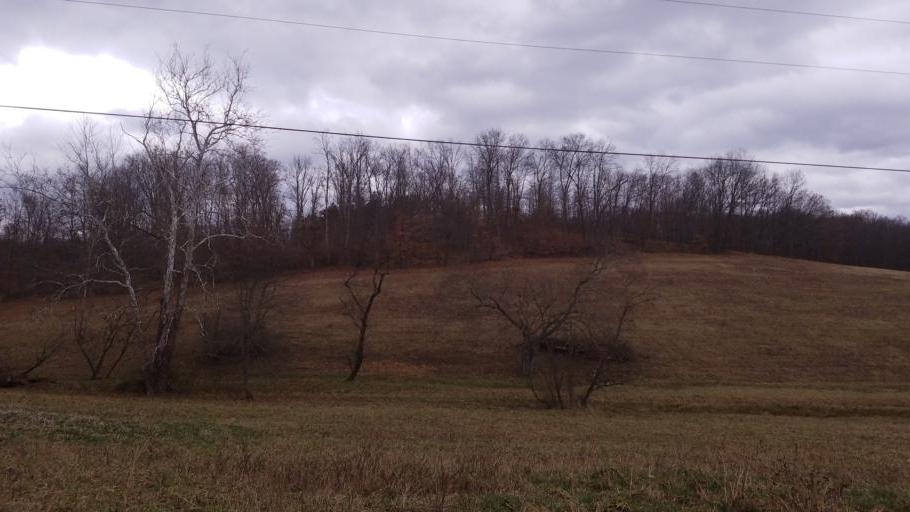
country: US
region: Ohio
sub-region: Licking County
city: Newark
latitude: 40.1739
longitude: -82.3188
